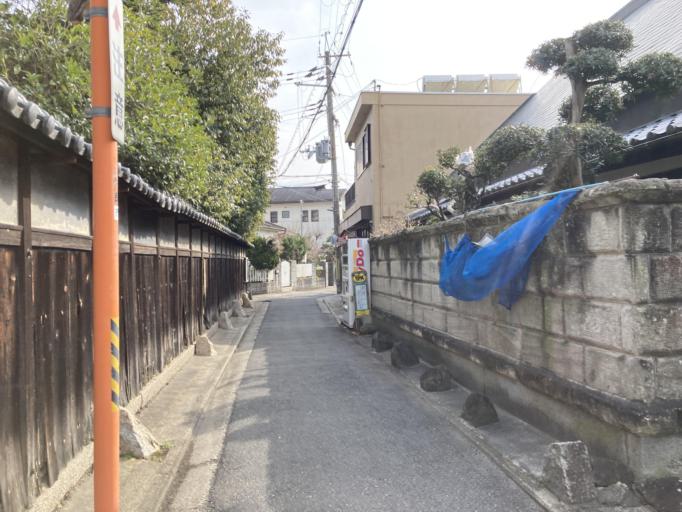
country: JP
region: Nara
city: Nara-shi
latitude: 34.6962
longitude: 135.7890
